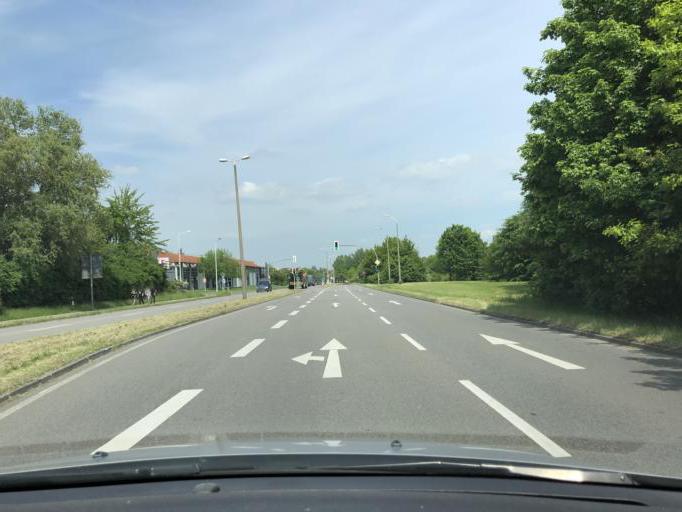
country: DE
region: Thuringia
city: Altenburg
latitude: 50.9953
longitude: 12.4229
